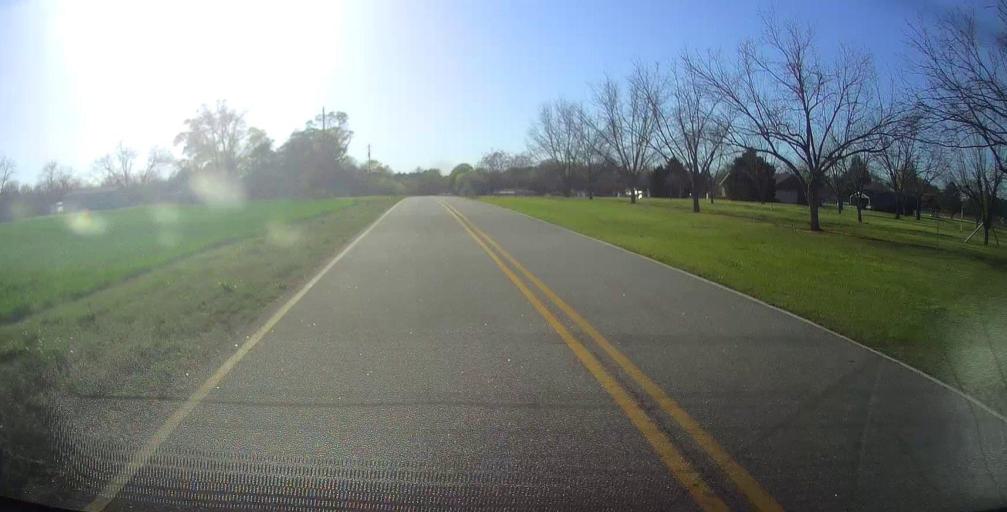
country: US
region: Georgia
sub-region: Houston County
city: Perry
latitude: 32.3639
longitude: -83.6598
